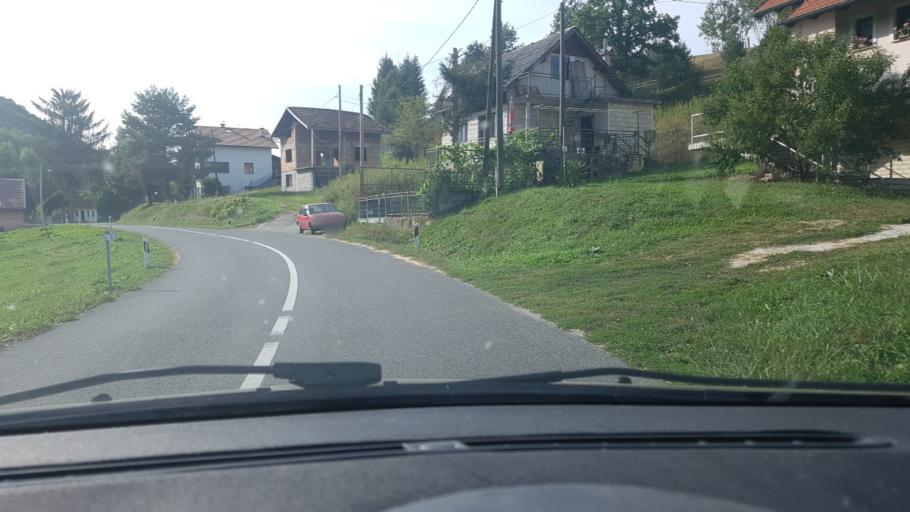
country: HR
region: Krapinsko-Zagorska
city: Mihovljan
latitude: 46.1195
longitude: 16.0000
